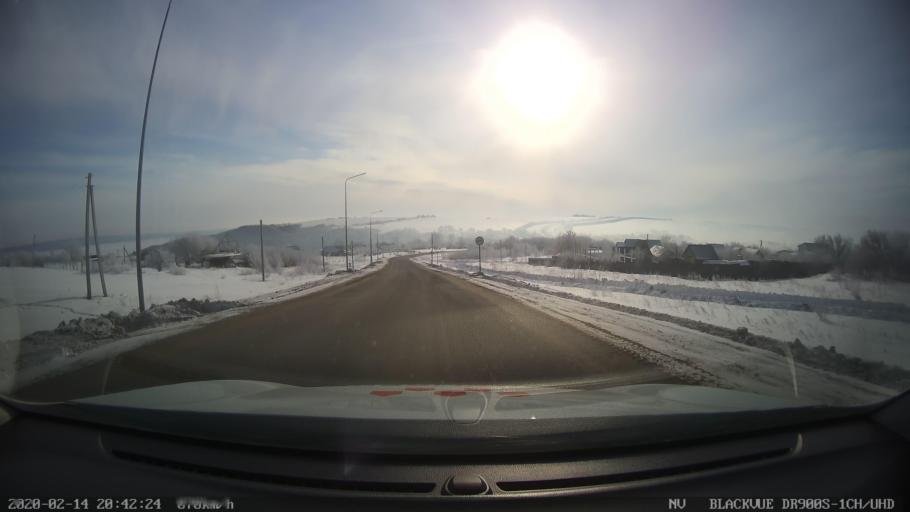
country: RU
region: Tatarstan
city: Kuybyshevskiy Zaton
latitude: 55.3173
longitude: 49.1420
